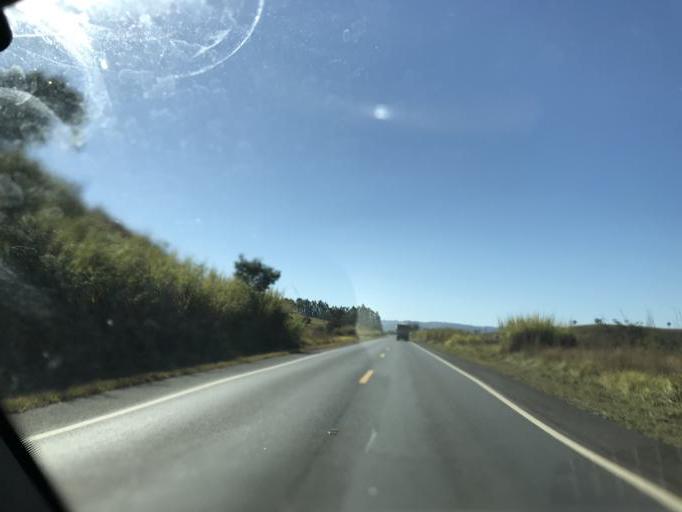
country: BR
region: Minas Gerais
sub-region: Bambui
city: Bambui
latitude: -19.8609
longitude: -45.9861
